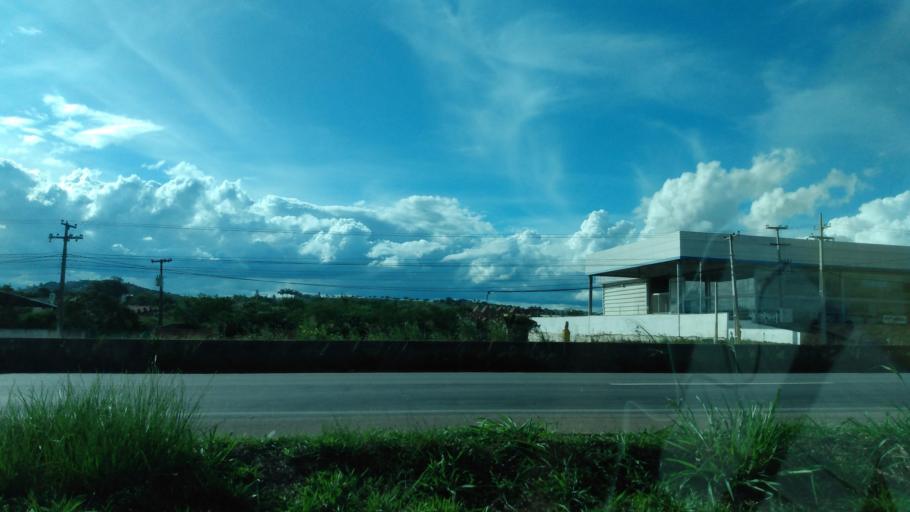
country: ET
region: Oromiya
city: Gore
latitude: 8.2016
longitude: 35.5924
